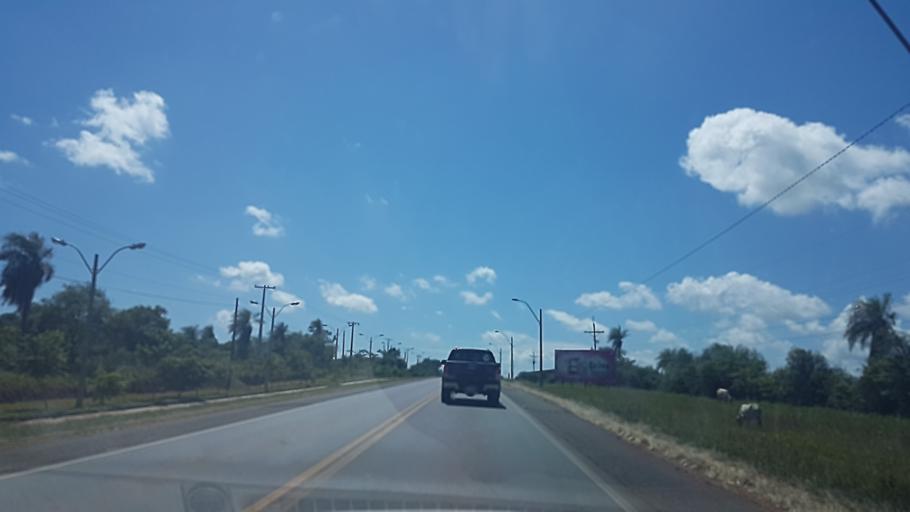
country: PY
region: Misiones
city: San Juan Bautista
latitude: -26.6725
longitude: -57.1239
